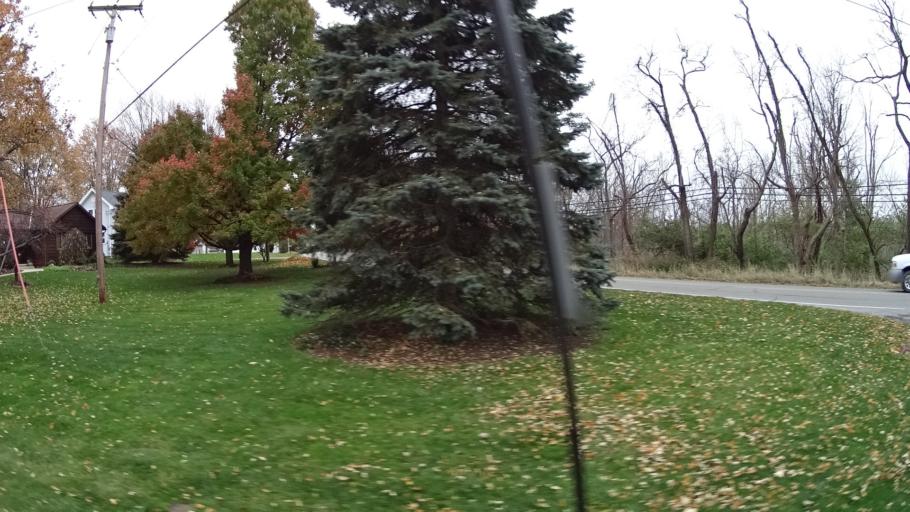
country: US
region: Ohio
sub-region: Lorain County
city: Sheffield
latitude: 41.4119
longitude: -82.0859
